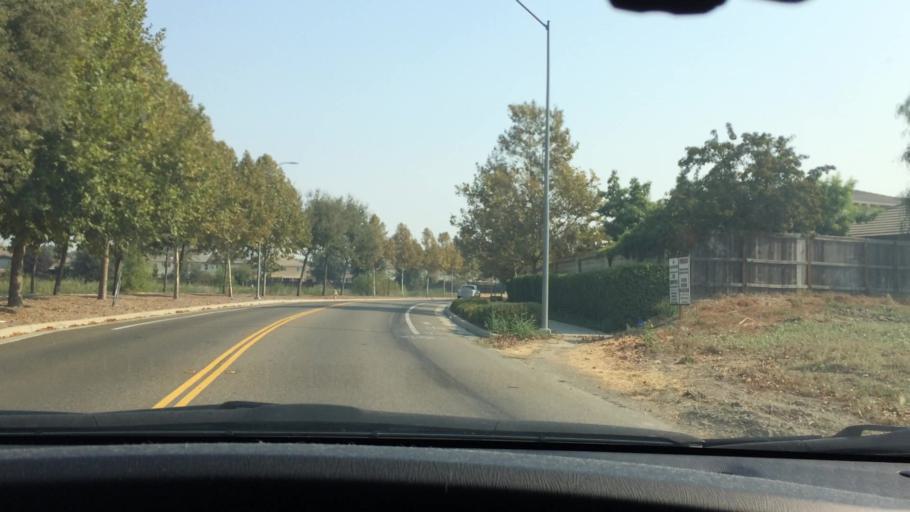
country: US
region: California
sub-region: Yolo County
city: West Sacramento
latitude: 38.5522
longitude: -121.5313
